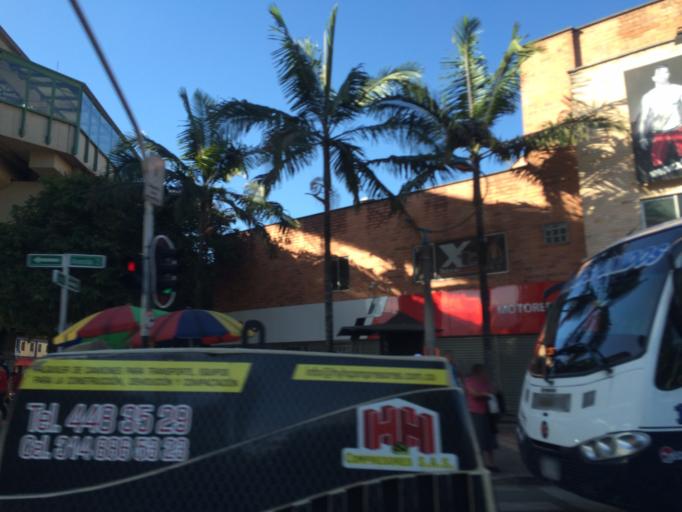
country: CO
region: Antioquia
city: Medellin
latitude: 6.2384
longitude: -75.5729
